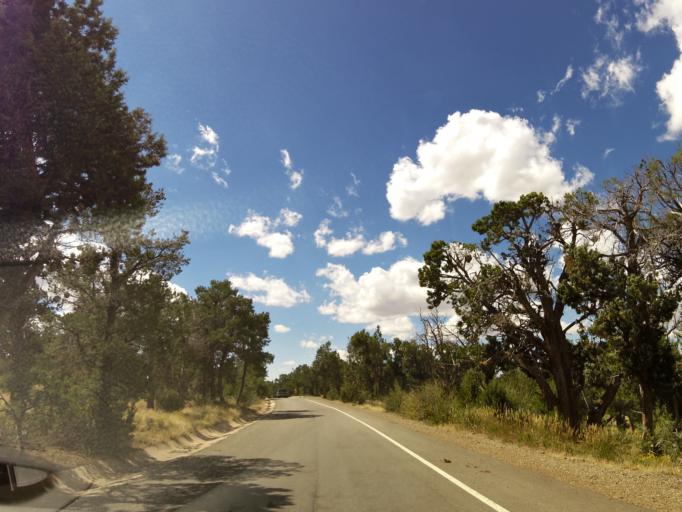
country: US
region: Colorado
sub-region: Montezuma County
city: Cortez
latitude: 37.1867
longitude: -108.4893
